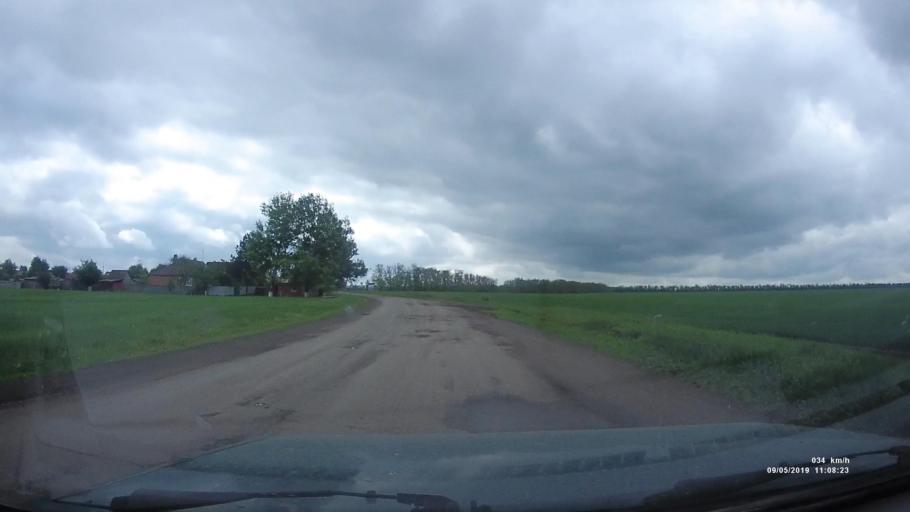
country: RU
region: Krasnodarskiy
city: Kanelovskaya
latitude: 46.7896
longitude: 39.2095
